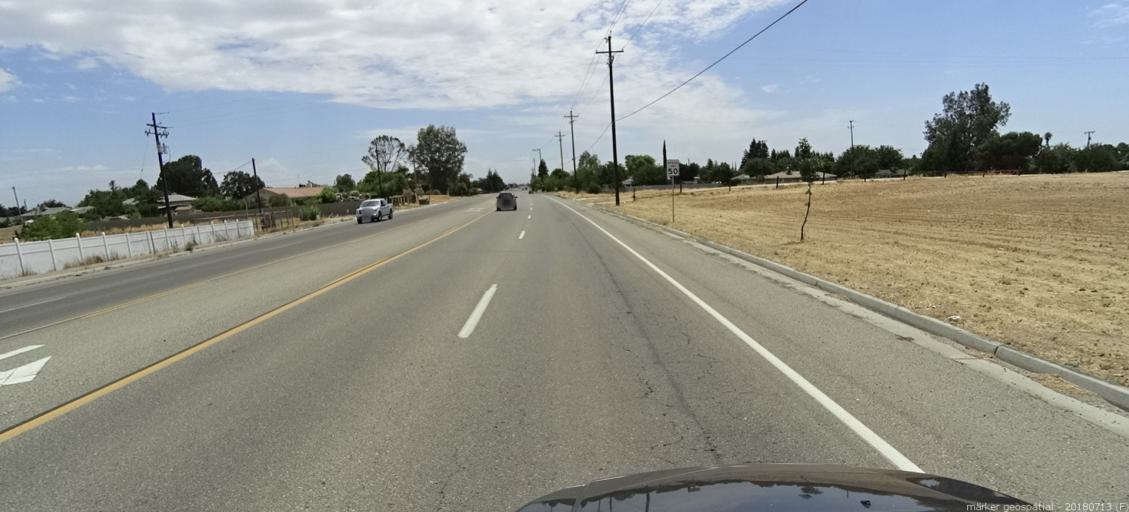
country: US
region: California
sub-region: Madera County
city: Madera Acres
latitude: 36.9963
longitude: -120.0841
